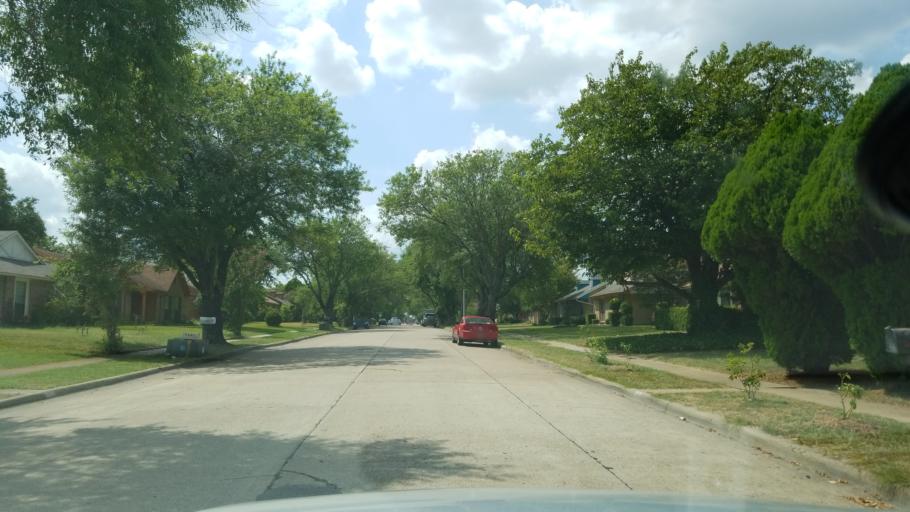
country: US
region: Texas
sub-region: Dallas County
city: Garland
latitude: 32.9234
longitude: -96.6673
